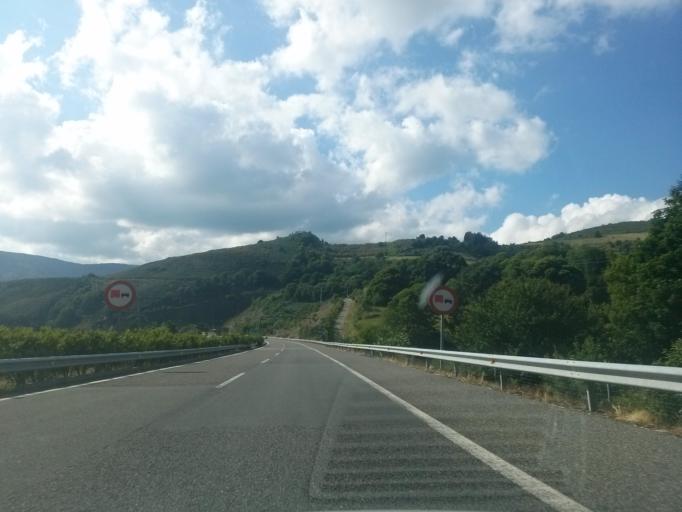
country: ES
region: Galicia
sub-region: Provincia de Lugo
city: San Roman
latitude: 42.7800
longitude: -7.1000
